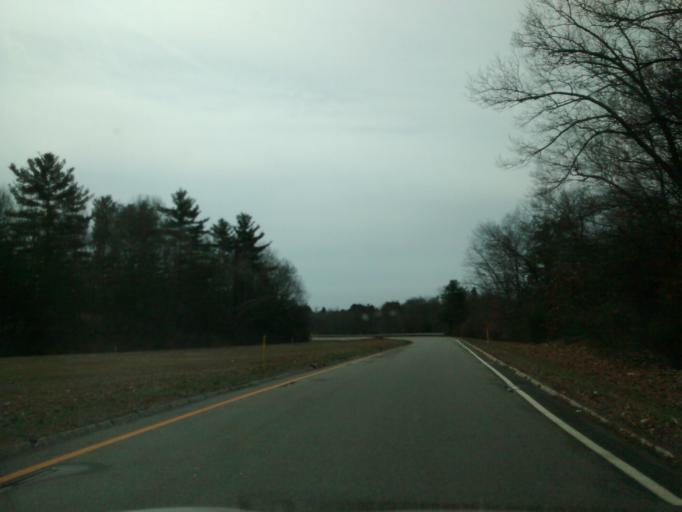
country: US
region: Massachusetts
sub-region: Worcester County
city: Oxford
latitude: 42.1194
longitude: -71.8563
